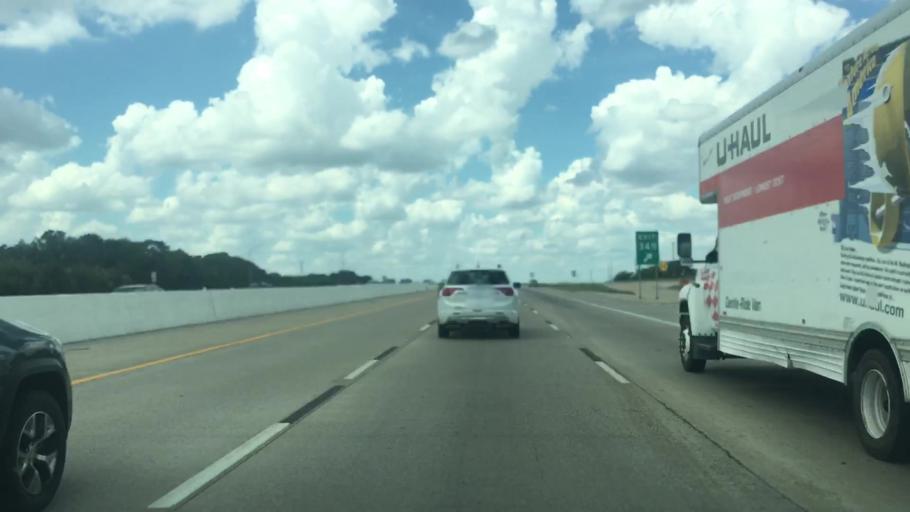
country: US
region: Texas
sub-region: McLennan County
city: West
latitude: 31.7333
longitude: -97.1031
